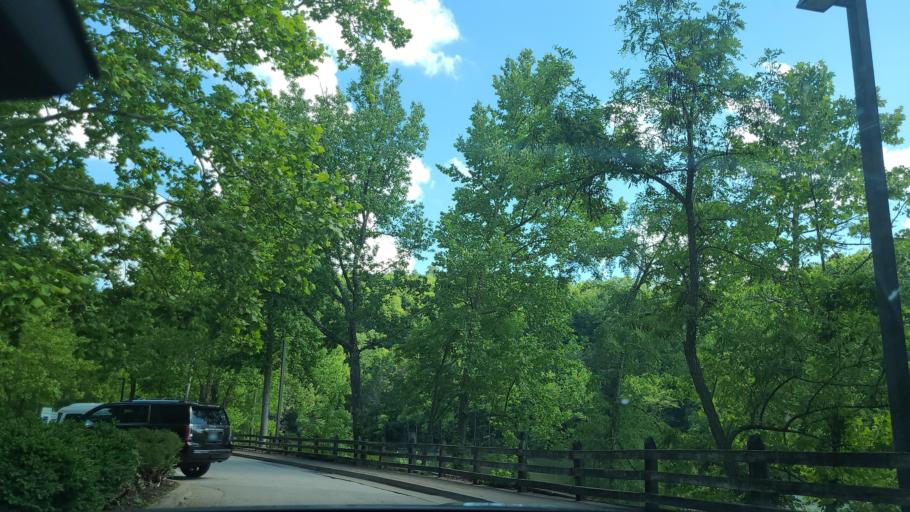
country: US
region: Kentucky
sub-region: McCreary County
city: Whitley City
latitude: 36.8376
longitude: -84.3436
